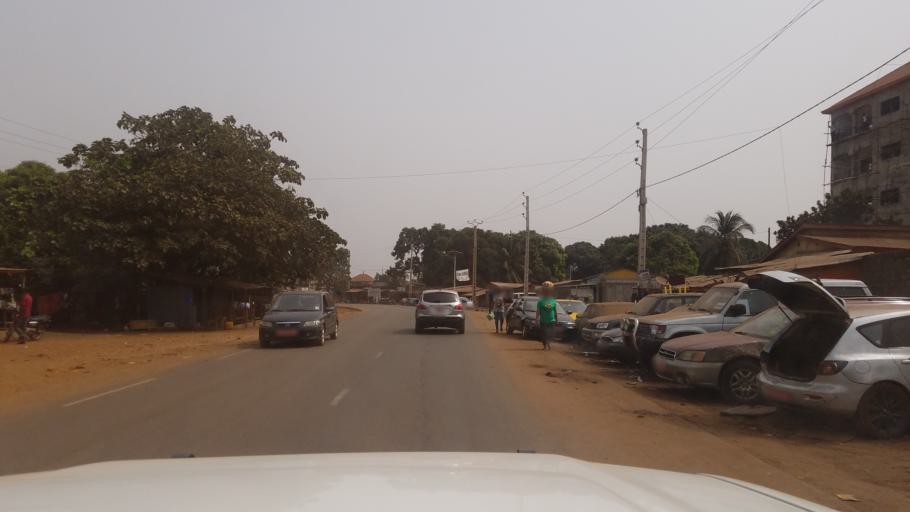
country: GN
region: Kindia
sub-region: Prefecture de Dubreka
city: Dubreka
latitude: 9.6697
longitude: -13.5849
